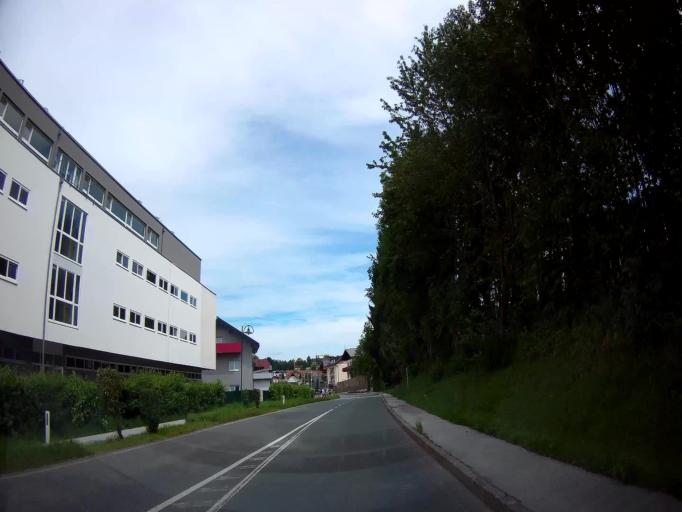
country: AT
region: Salzburg
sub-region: Politischer Bezirk Salzburg-Umgebung
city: Hallwang
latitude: 47.8476
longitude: 13.1038
